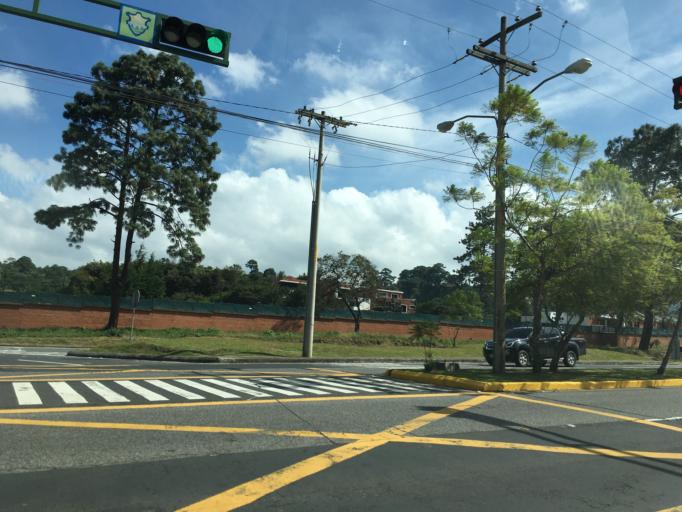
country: GT
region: Guatemala
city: Santa Catarina Pinula
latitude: 14.6034
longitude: -90.4840
